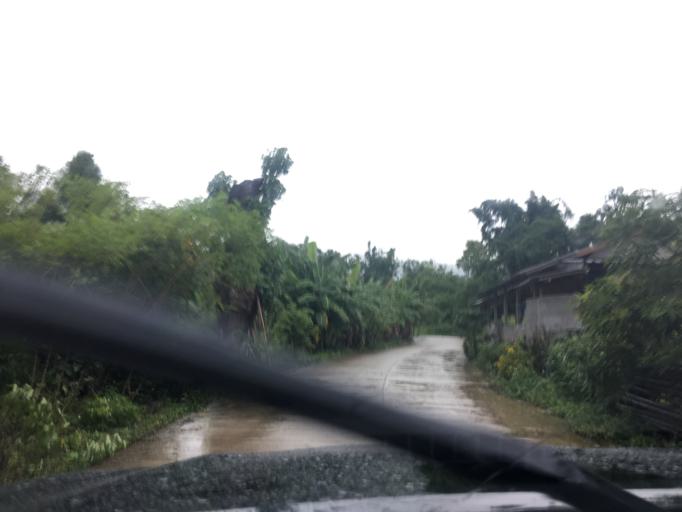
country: TH
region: Chiang Rai
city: Chiang Khong
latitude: 20.3002
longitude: 100.2527
